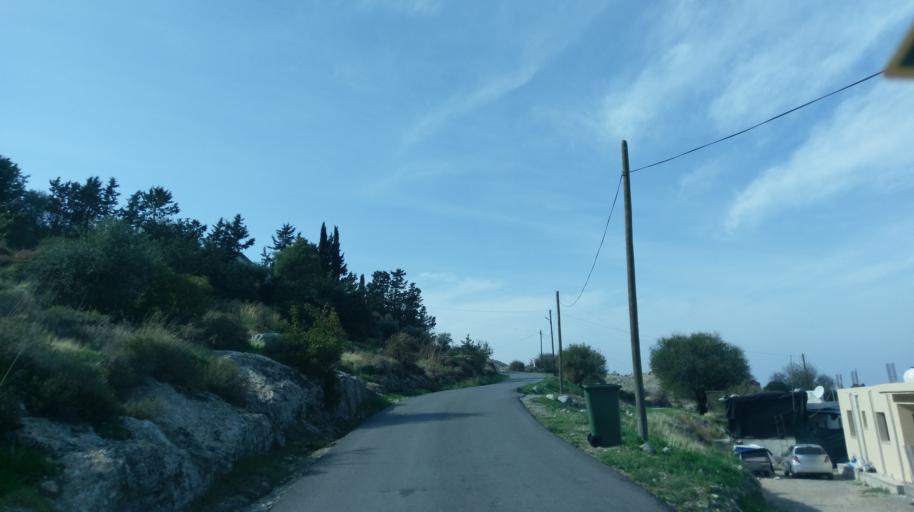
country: CY
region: Keryneia
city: Lapithos
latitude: 35.3432
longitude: 33.1201
